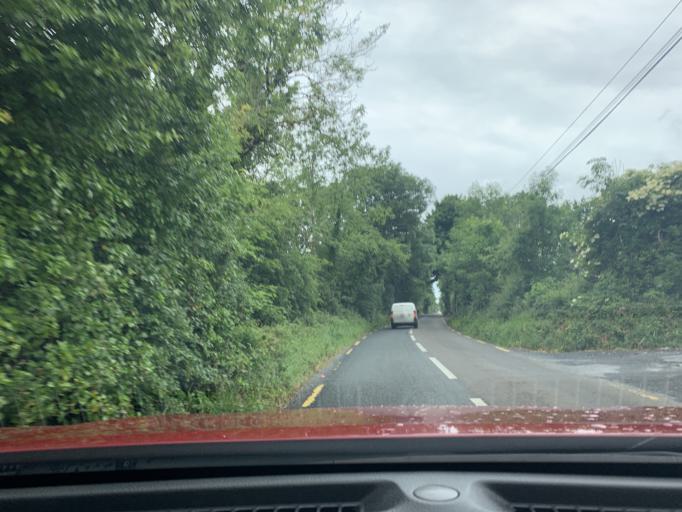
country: IE
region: Connaught
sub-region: Sligo
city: Sligo
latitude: 54.3135
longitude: -8.4671
